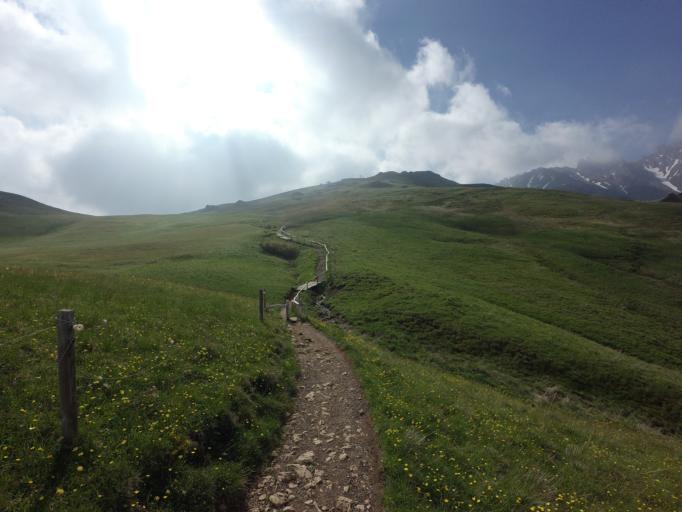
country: IT
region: Trentino-Alto Adige
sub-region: Bolzano
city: Ortisei
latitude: 46.5165
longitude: 11.6336
